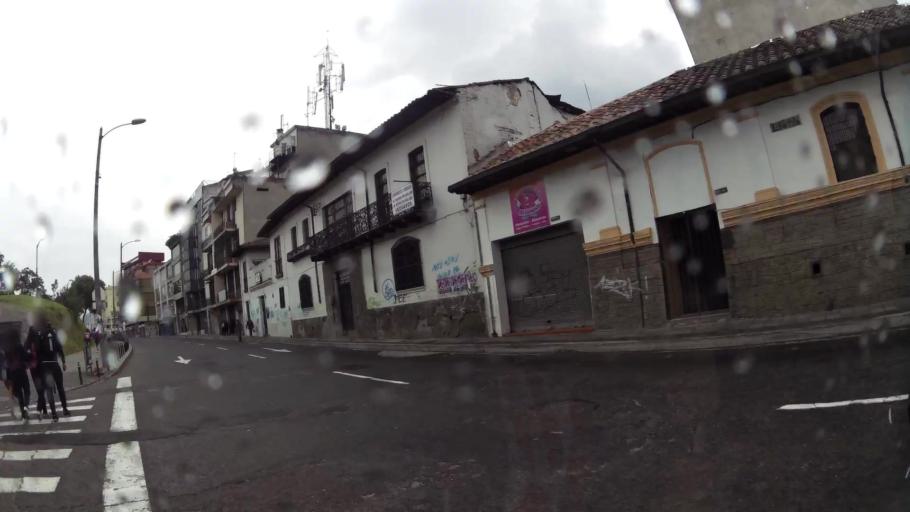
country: EC
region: Pichincha
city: Quito
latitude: -0.2130
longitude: -78.5018
